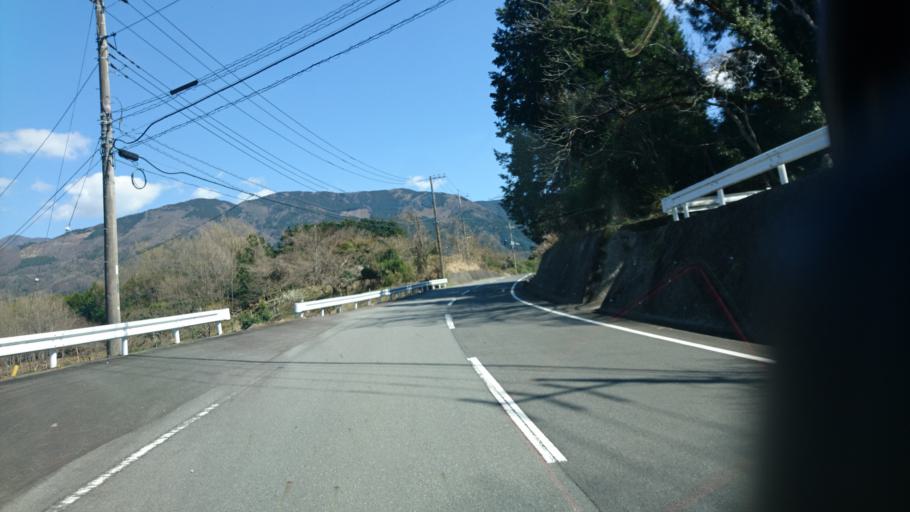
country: JP
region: Shizuoka
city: Fujinomiya
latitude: 35.3426
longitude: 138.4390
